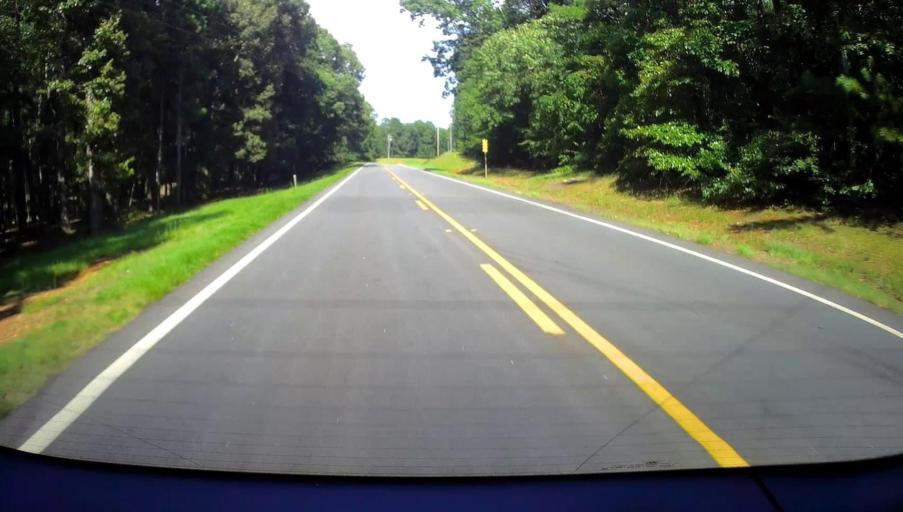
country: US
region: Georgia
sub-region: Upson County
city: Hannahs Mill
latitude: 32.9067
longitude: -84.3704
